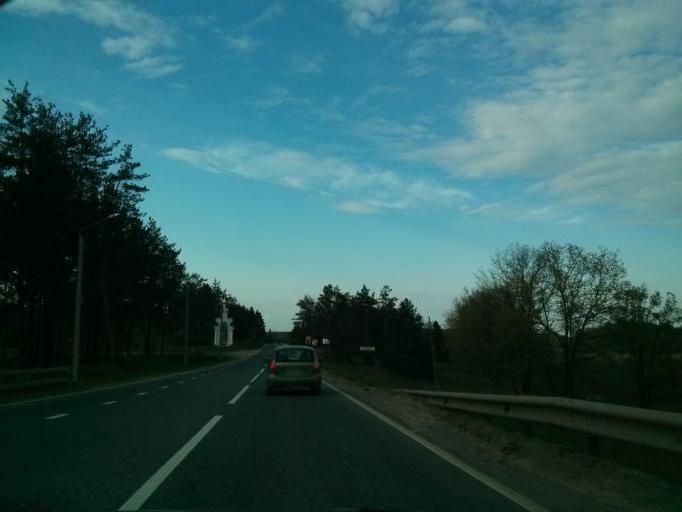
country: RU
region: Nizjnij Novgorod
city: Navashino
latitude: 55.5876
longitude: 42.1503
